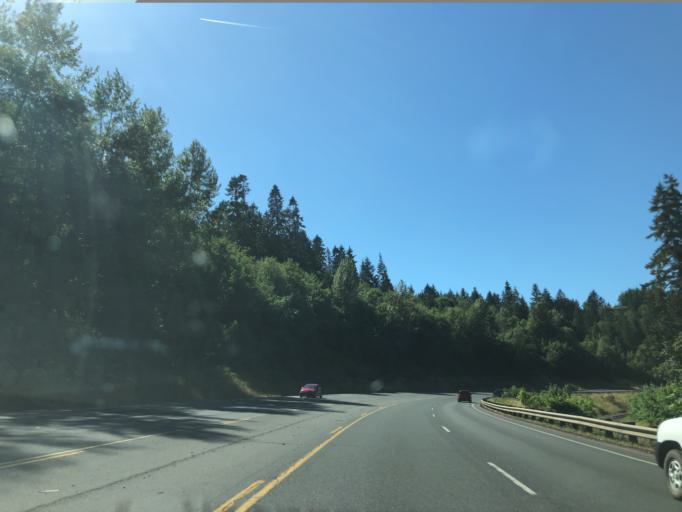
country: US
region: Oregon
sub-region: Linn County
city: Sweet Home
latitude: 44.4052
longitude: -122.7608
